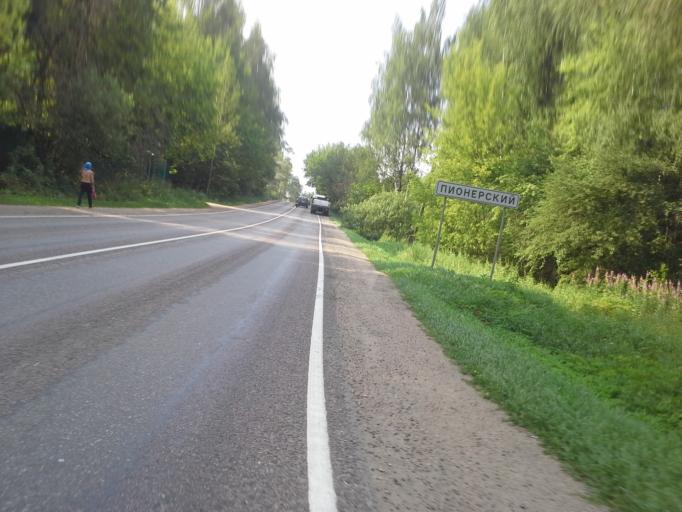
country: RU
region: Moskovskaya
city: Istra
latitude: 55.8857
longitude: 36.7985
